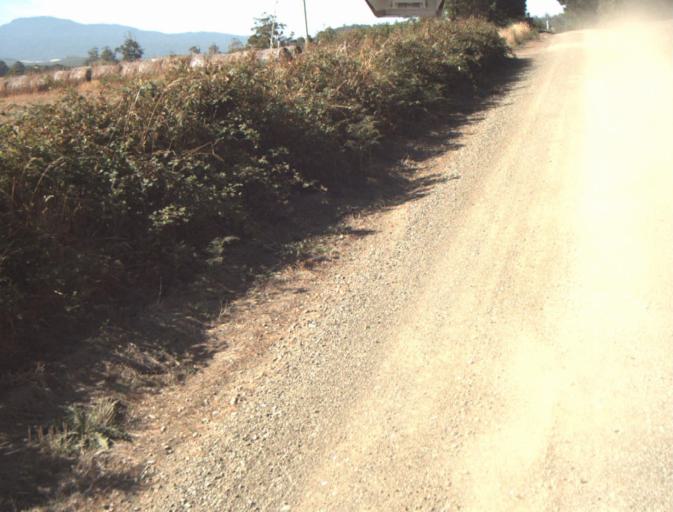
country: AU
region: Tasmania
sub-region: Launceston
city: Mayfield
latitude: -41.1664
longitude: 147.2120
